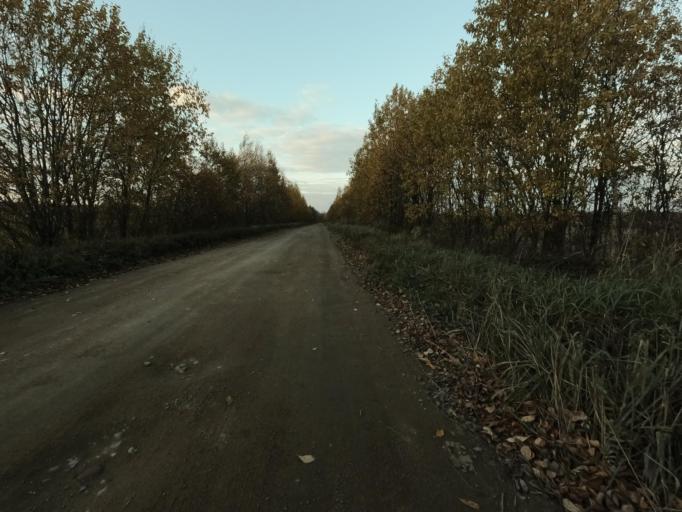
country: RU
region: Leningrad
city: Mga
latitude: 59.8021
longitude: 31.2005
